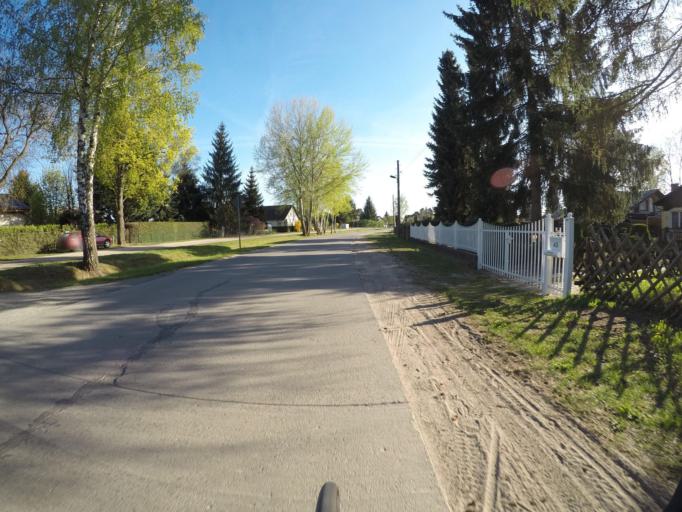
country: DE
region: Brandenburg
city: Neuenhagen
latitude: 52.5126
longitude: 13.7231
